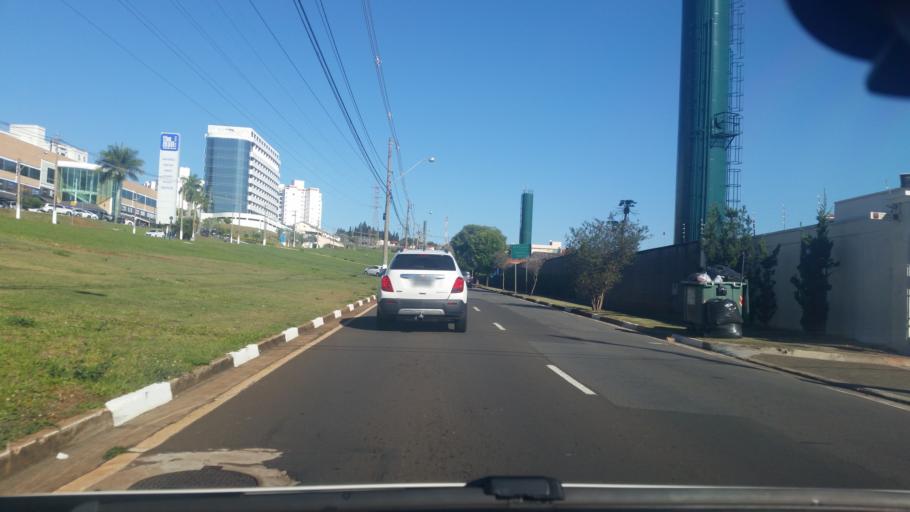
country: BR
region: Sao Paulo
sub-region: Campinas
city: Campinas
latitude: -22.8552
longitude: -47.0574
